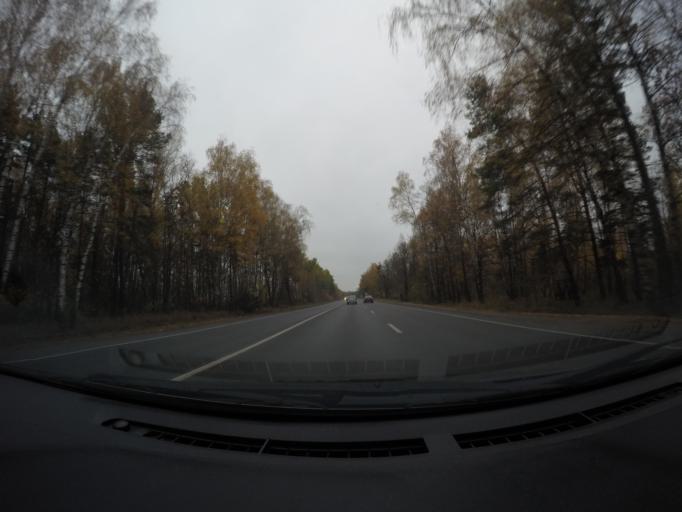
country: RU
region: Moskovskaya
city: Malyshevo
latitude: 55.4509
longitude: 38.3245
